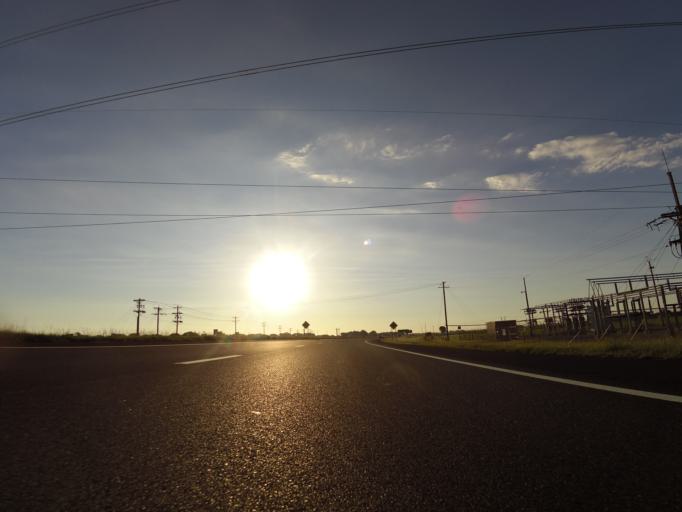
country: US
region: Kansas
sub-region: Sedgwick County
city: Colwich
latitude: 37.8248
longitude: -97.5230
